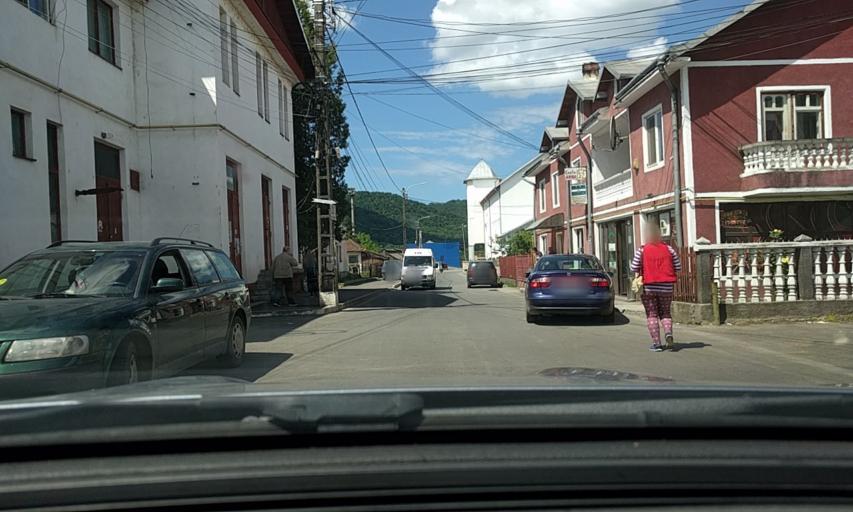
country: RO
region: Bistrita-Nasaud
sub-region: Oras Nasaud
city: Nasaud
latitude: 47.2815
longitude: 24.4109
